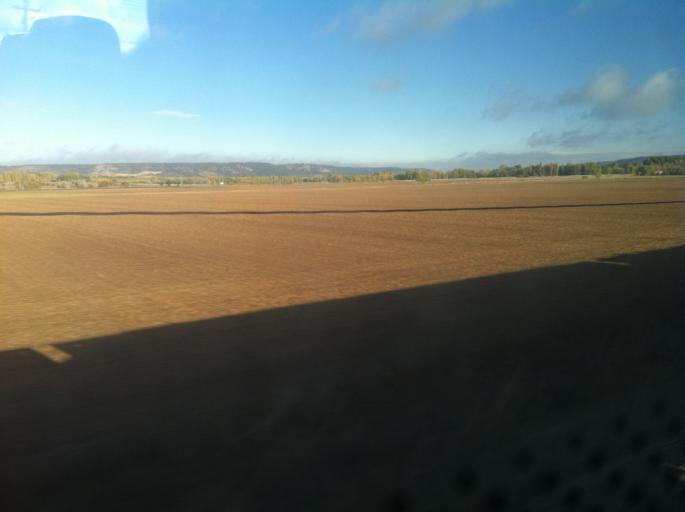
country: ES
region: Castille and Leon
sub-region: Provincia de Palencia
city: Hornillos de Cerrato
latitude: 42.0317
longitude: -4.2743
